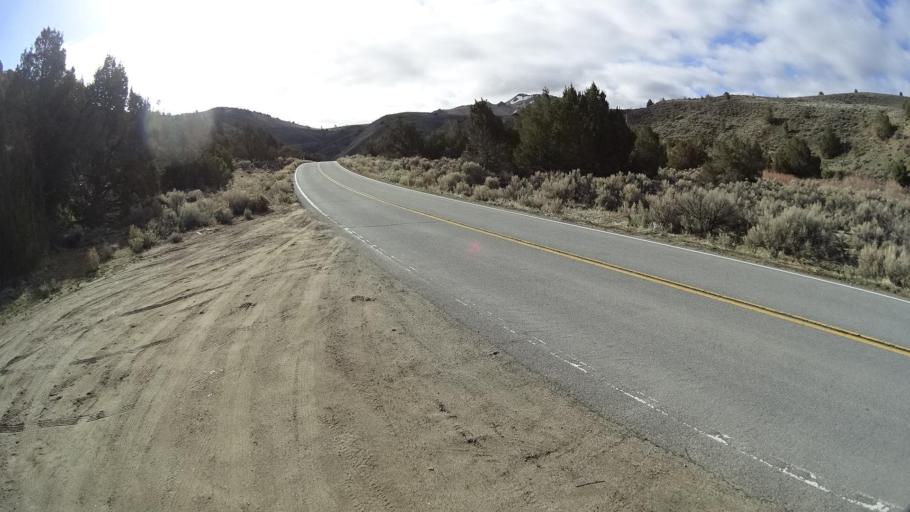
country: US
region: Nevada
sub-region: Washoe County
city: Cold Springs
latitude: 39.9067
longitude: -120.0016
